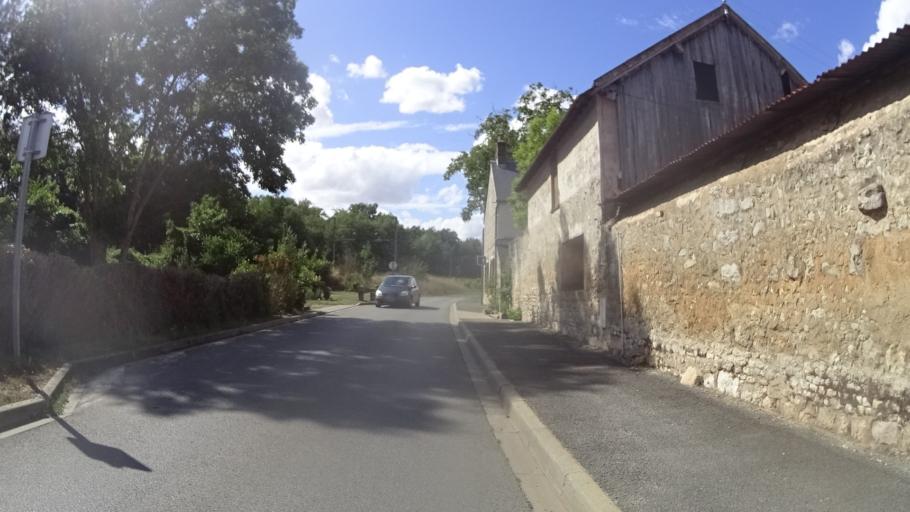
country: FR
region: Ile-de-France
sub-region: Departement de l'Essonne
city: La Ferte-Alais
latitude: 48.4547
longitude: 2.3605
